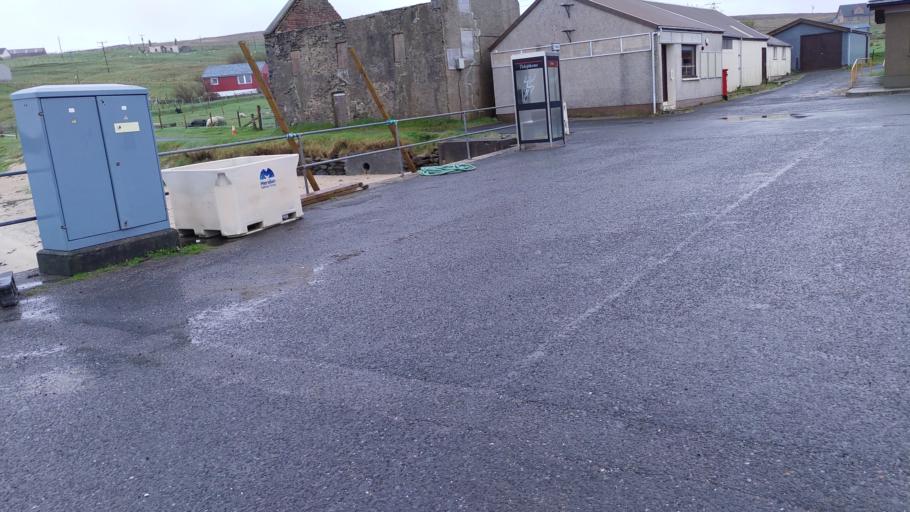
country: GB
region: Scotland
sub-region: Shetland Islands
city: Shetland
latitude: 60.5979
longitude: -1.0591
